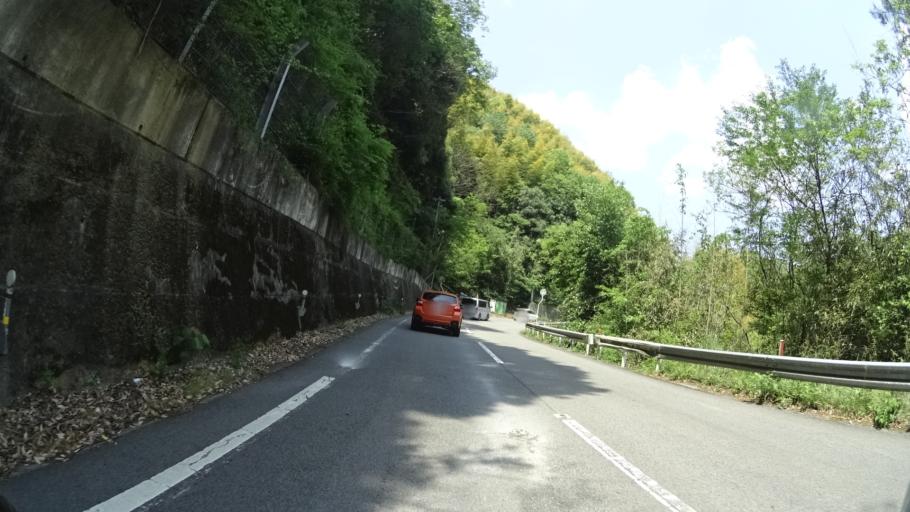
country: JP
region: Ehime
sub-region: Shikoku-chuo Shi
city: Matsuyama
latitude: 33.8760
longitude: 132.8354
